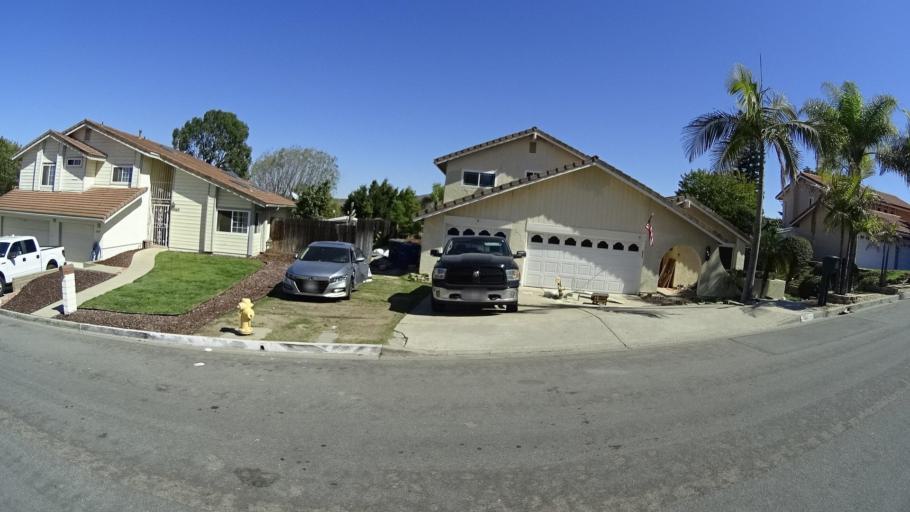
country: US
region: California
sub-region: San Diego County
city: Bonita
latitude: 32.6727
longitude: -117.0017
